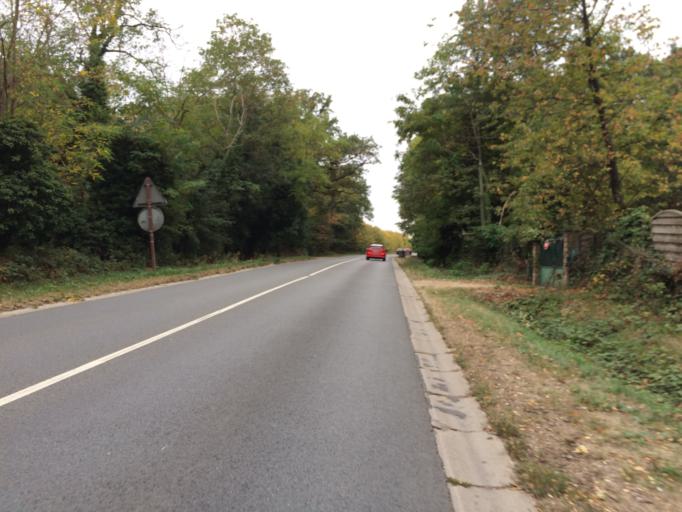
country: FR
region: Ile-de-France
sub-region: Departement de l'Essonne
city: Villejust
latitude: 48.6926
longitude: 2.2346
